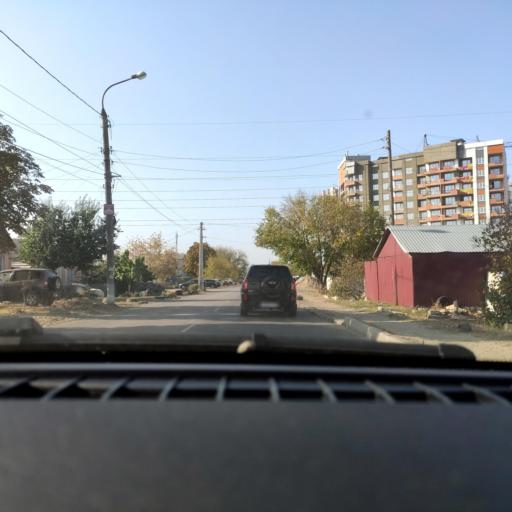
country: RU
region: Voronezj
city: Maslovka
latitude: 51.6103
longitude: 39.2197
